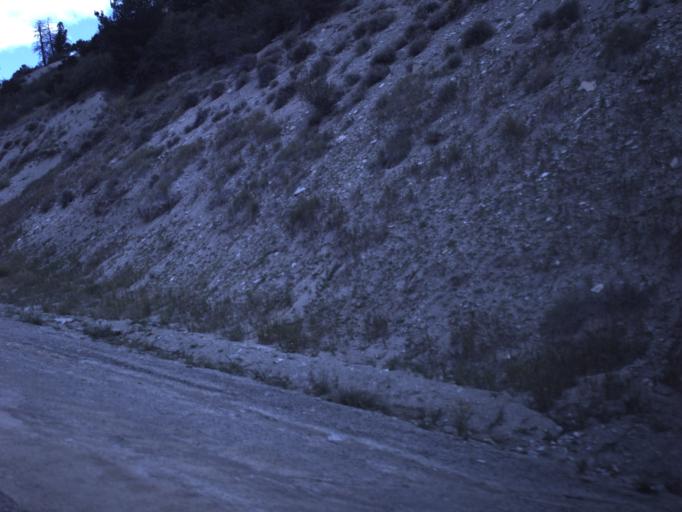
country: US
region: Utah
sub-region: Carbon County
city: Helper
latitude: 39.9030
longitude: -110.7310
